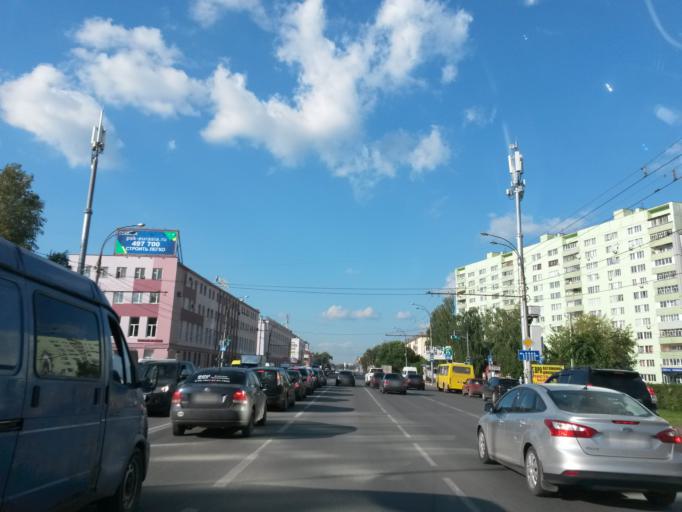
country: RU
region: Ivanovo
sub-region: Gorod Ivanovo
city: Ivanovo
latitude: 56.9753
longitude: 40.9749
